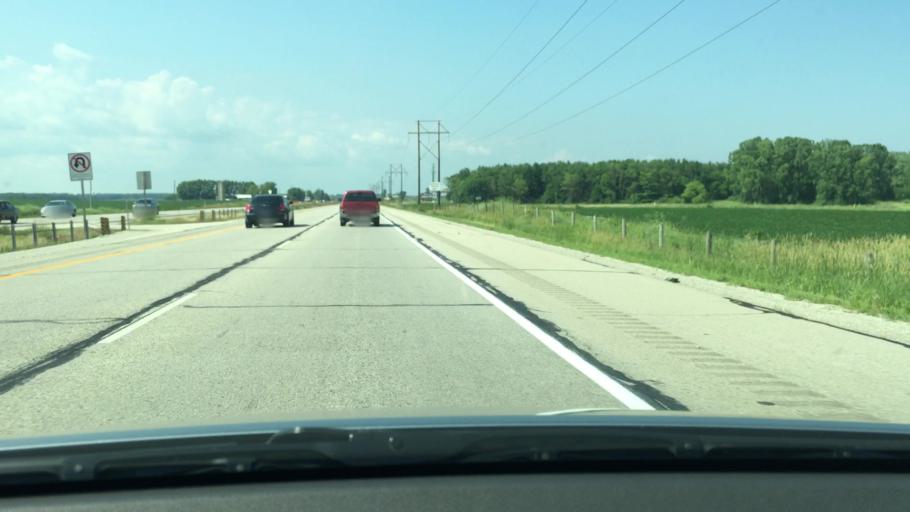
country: US
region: Wisconsin
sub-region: Fond du Lac County
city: Rosendale
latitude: 43.8975
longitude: -88.5835
